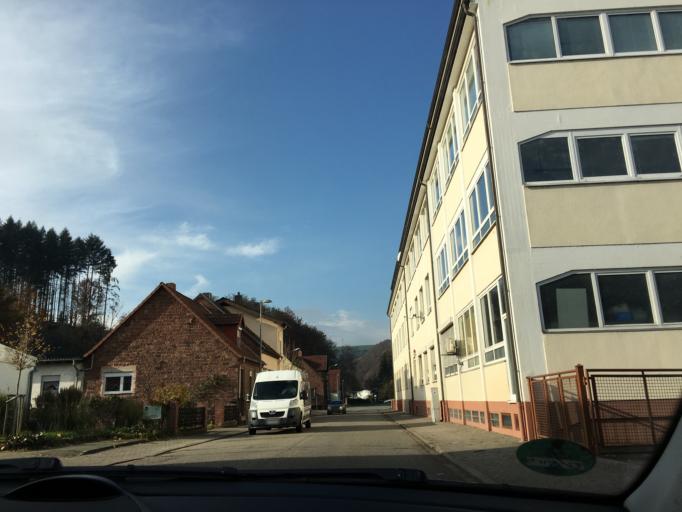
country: DE
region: Rheinland-Pfalz
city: Waldfischbach-Burgalben
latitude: 49.2812
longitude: 7.6382
